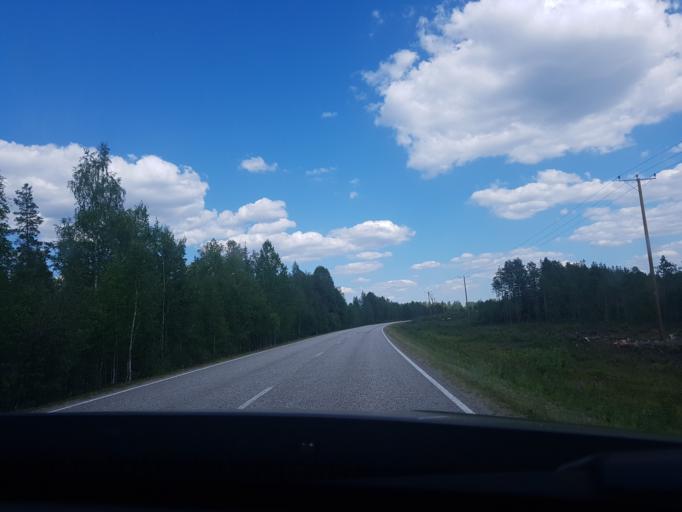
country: FI
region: Kainuu
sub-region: Kehys-Kainuu
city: Kuhmo
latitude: 64.2138
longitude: 29.7634
